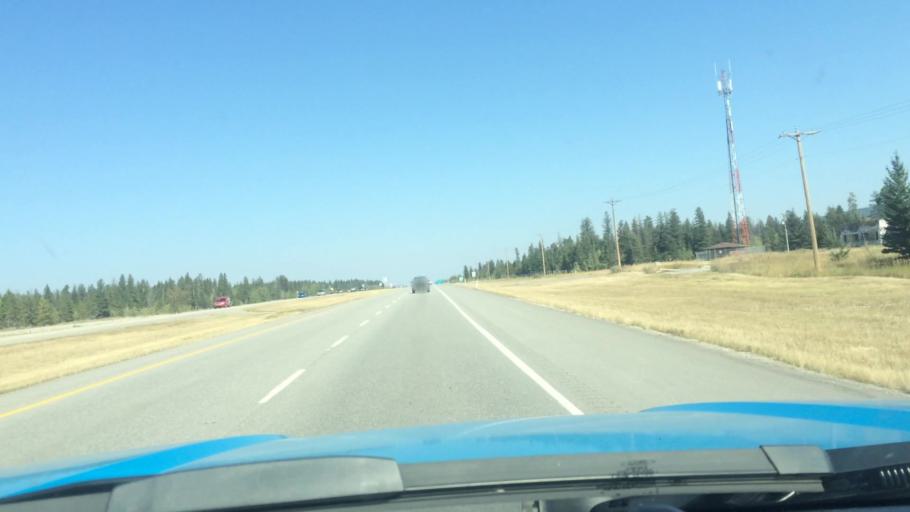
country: CA
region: Alberta
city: Canmore
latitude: 51.0926
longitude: -115.0484
